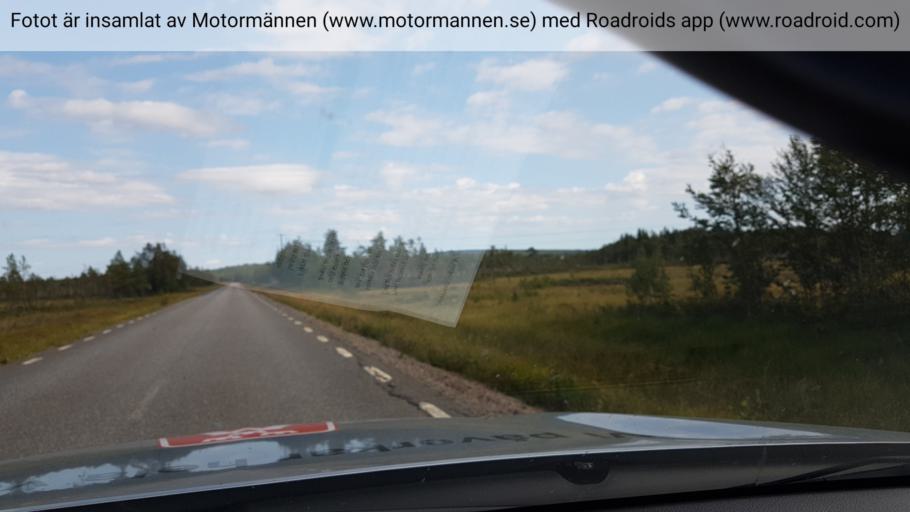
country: SE
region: Vaesterbotten
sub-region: Skelleftea Kommun
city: Boliden
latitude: 65.3150
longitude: 20.2666
